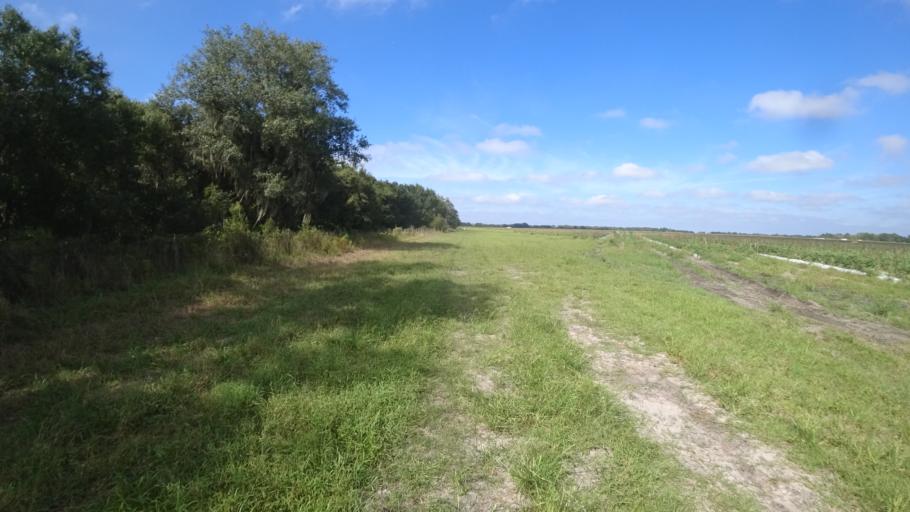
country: US
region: Florida
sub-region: DeSoto County
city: Arcadia
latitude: 27.2796
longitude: -82.0820
